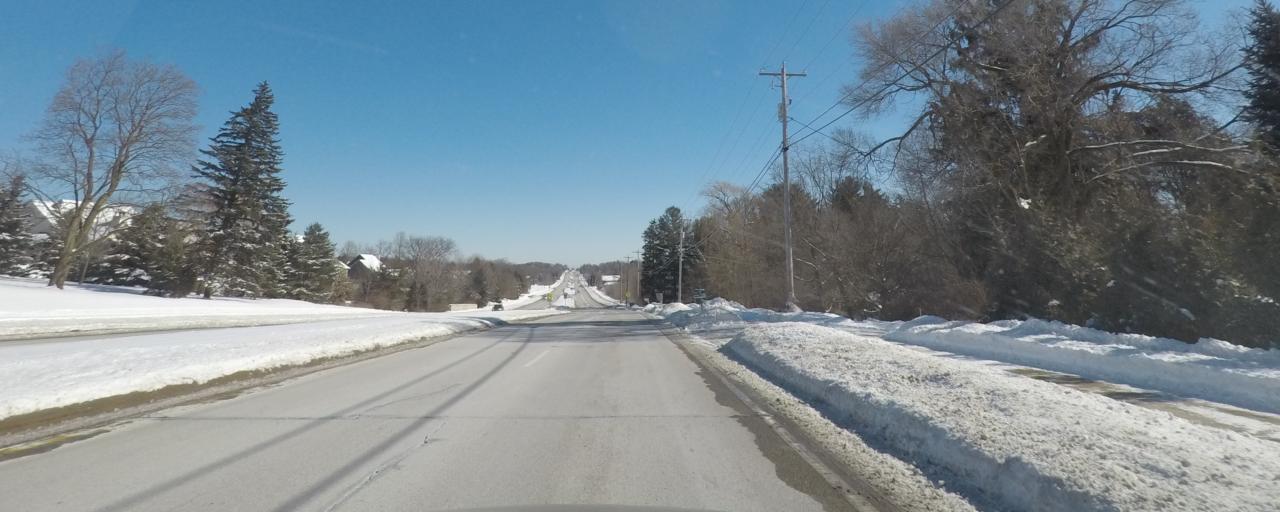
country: US
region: Wisconsin
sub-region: Waukesha County
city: New Berlin
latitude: 43.0170
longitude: -88.1444
